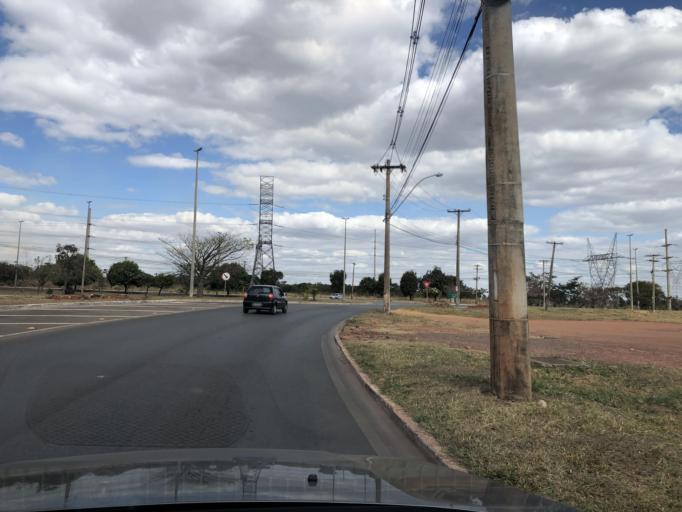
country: BR
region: Federal District
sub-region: Brasilia
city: Brasilia
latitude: -15.8938
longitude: -48.1388
